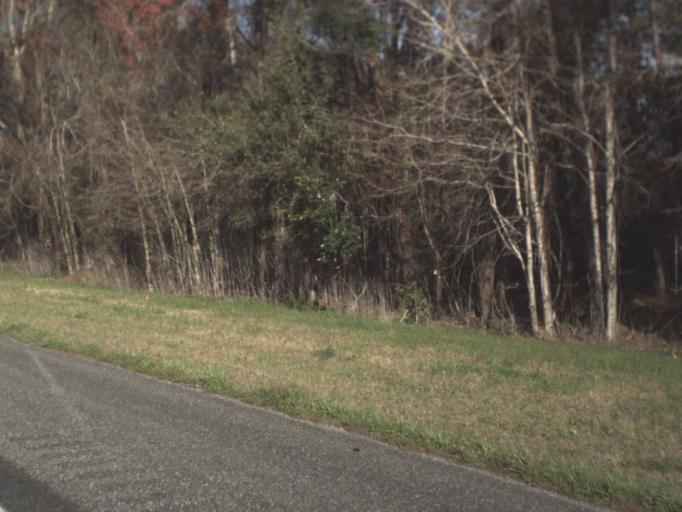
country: US
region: Florida
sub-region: Jefferson County
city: Monticello
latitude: 30.4729
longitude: -83.8369
